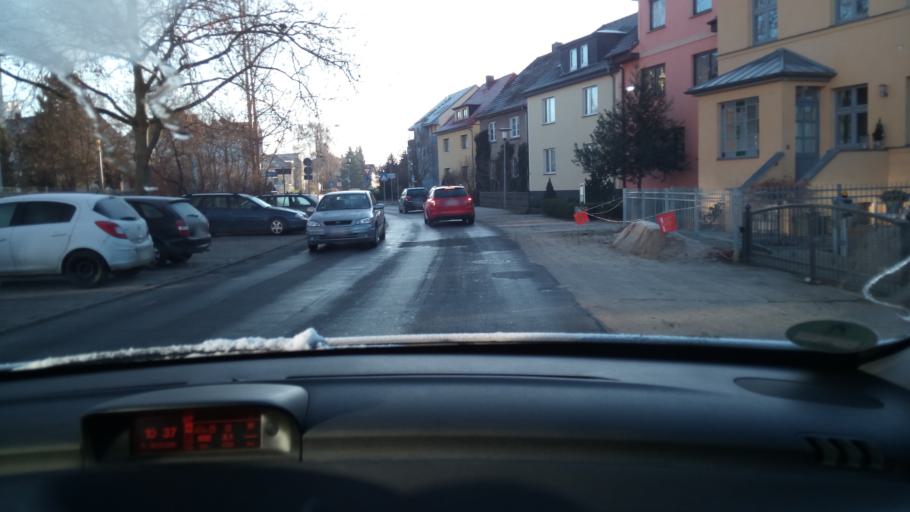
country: DE
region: Mecklenburg-Vorpommern
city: Neubrandenburg
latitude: 53.5615
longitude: 13.2480
